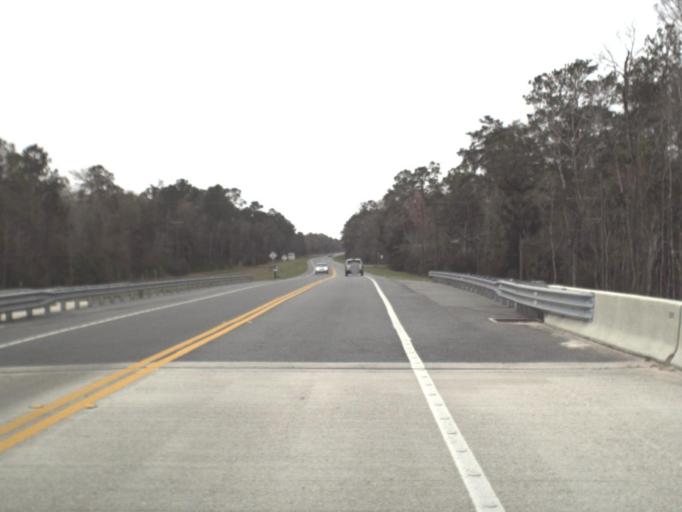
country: US
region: Florida
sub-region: Wakulla County
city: Crawfordville
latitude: 30.1755
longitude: -84.2456
